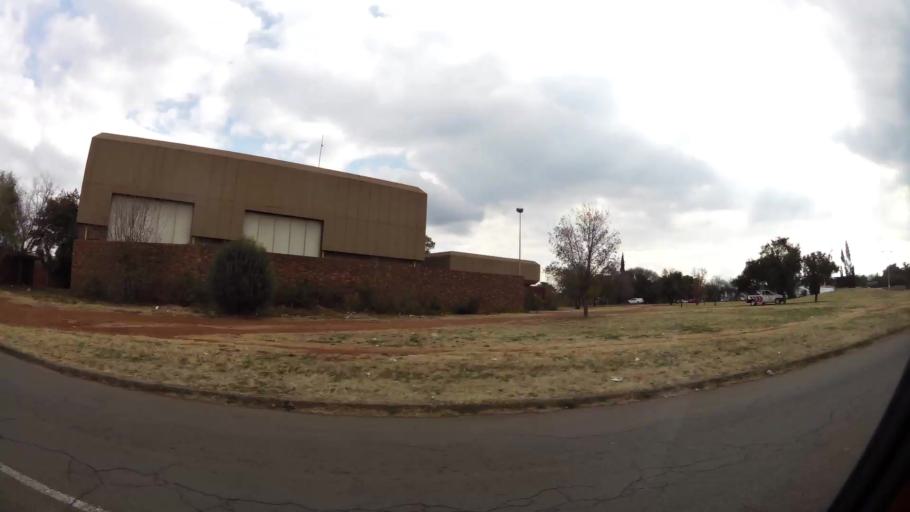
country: ZA
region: Gauteng
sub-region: Sedibeng District Municipality
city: Vanderbijlpark
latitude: -26.7234
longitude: 27.8370
